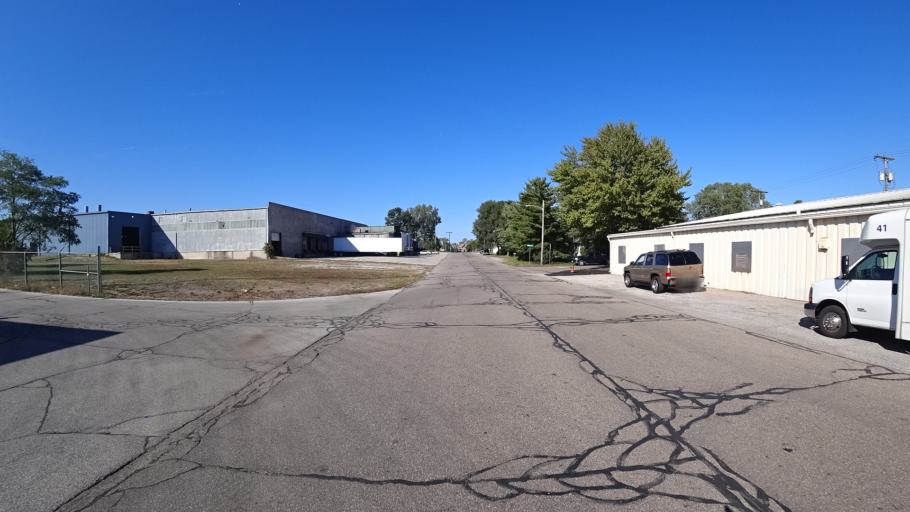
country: US
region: Indiana
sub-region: LaPorte County
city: Michigan City
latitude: 41.7032
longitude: -86.9061
